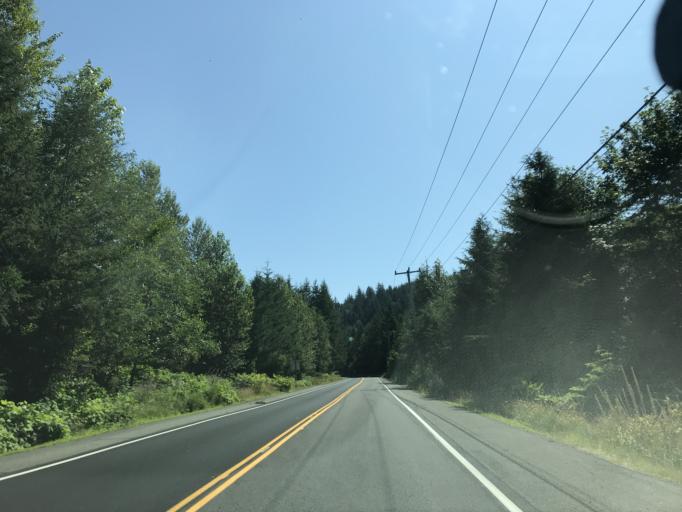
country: US
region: Washington
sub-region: King County
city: Ravensdale
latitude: 47.3564
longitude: -121.8907
